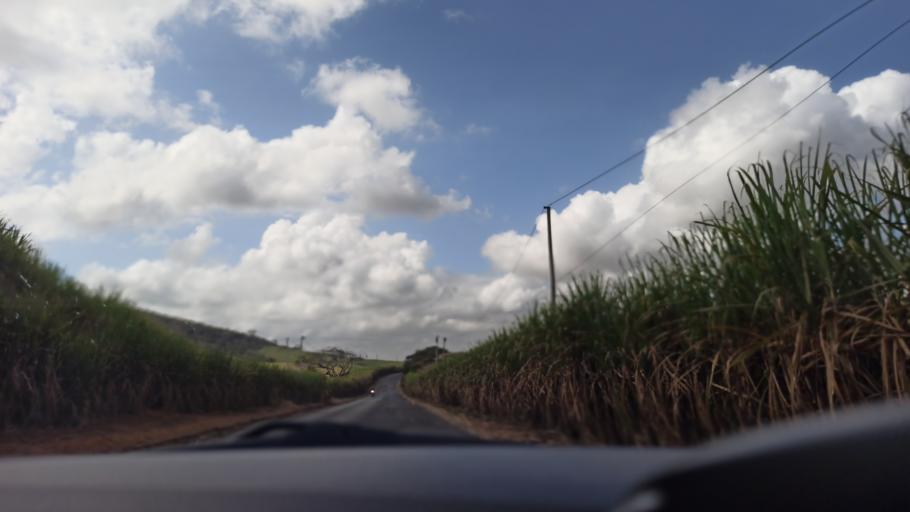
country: BR
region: Paraiba
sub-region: Juripiranga
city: Juripiranga
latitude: -7.3960
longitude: -35.2574
